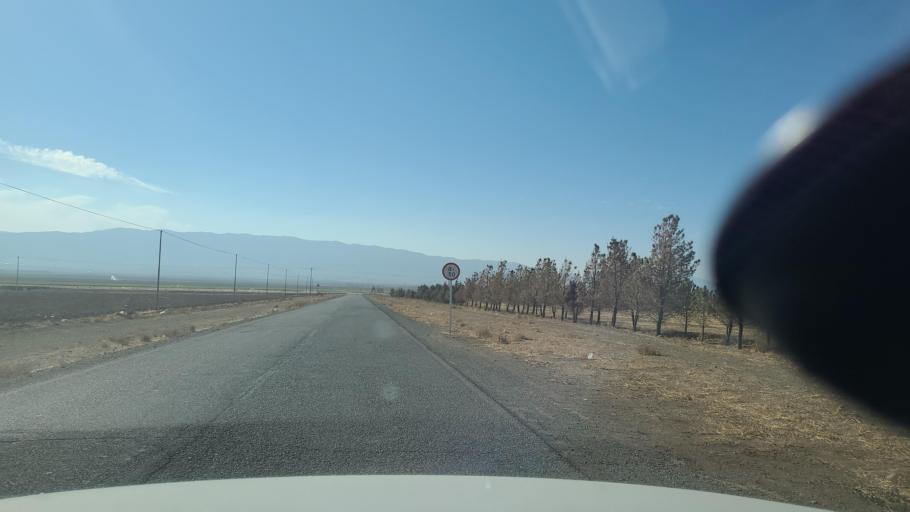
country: IR
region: Razavi Khorasan
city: Dowlatabad
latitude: 35.6026
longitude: 59.4615
